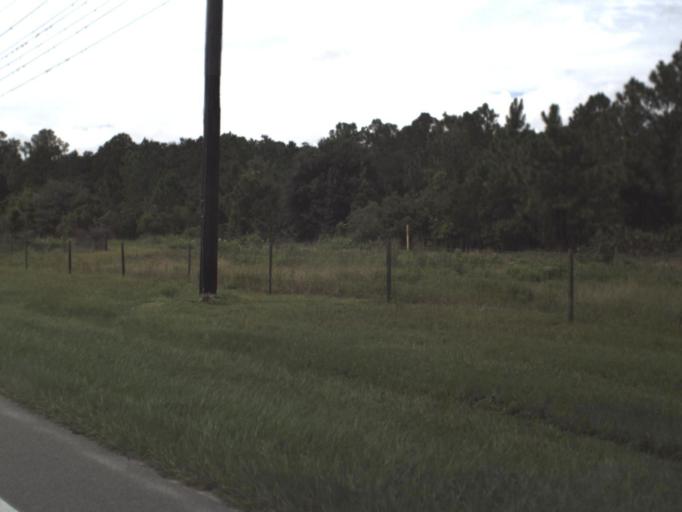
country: US
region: Florida
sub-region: Hillsborough County
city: Wimauma
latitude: 27.5902
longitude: -82.1249
